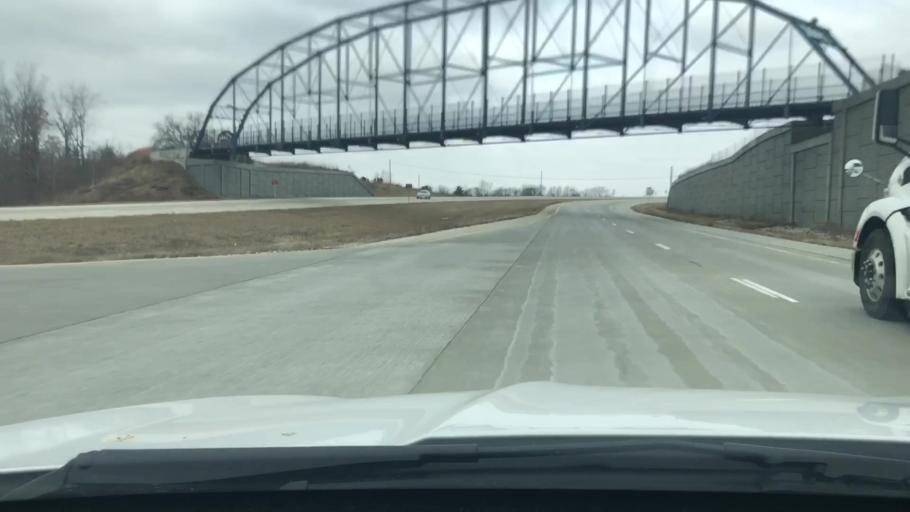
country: US
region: Indiana
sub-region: Carroll County
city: Delphi
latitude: 40.5935
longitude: -86.6543
